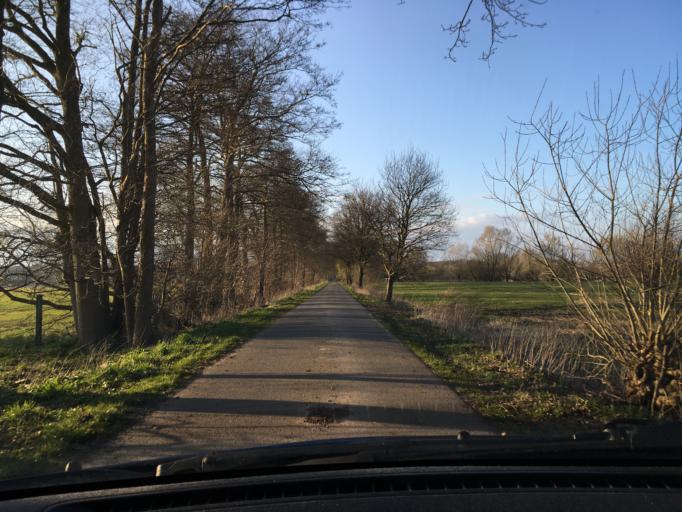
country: DE
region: Lower Saxony
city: Hittbergen
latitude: 53.3238
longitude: 10.6278
